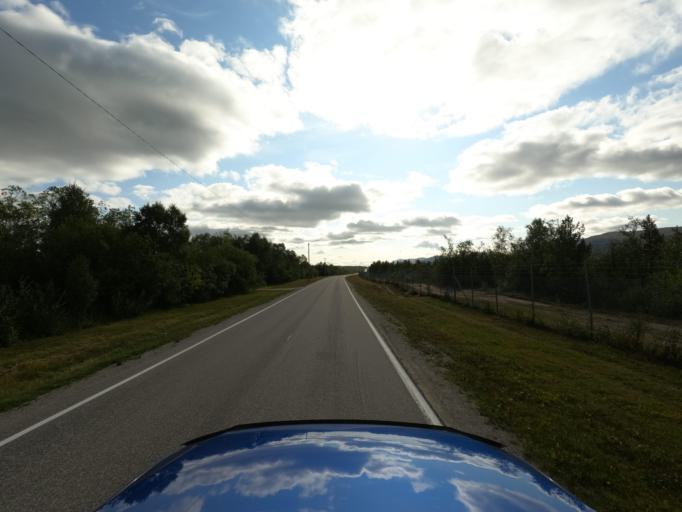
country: NO
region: Finnmark Fylke
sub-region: Porsanger
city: Lakselv
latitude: 70.0598
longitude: 24.9838
